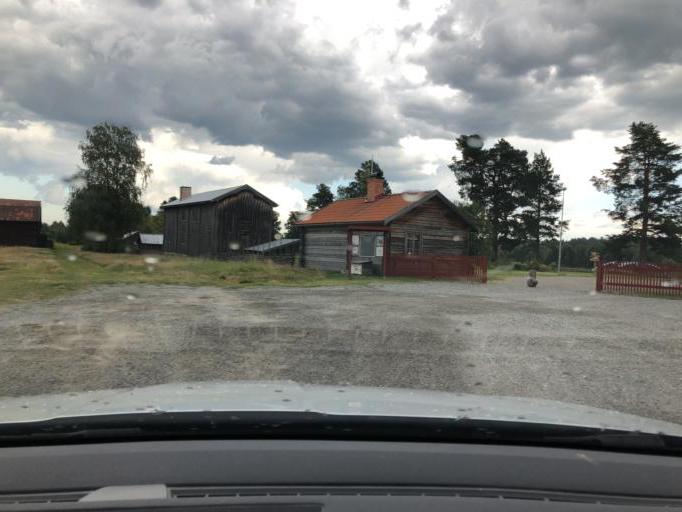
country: SE
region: Gaevleborg
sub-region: Ljusdals Kommun
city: Farila
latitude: 61.8067
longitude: 15.8472
